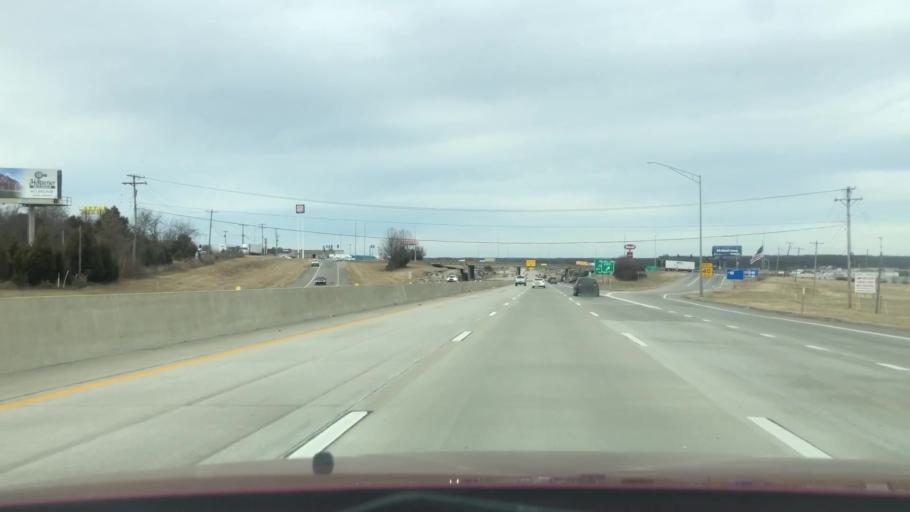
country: US
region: Missouri
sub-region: Greene County
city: Springfield
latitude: 37.2361
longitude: -93.2248
